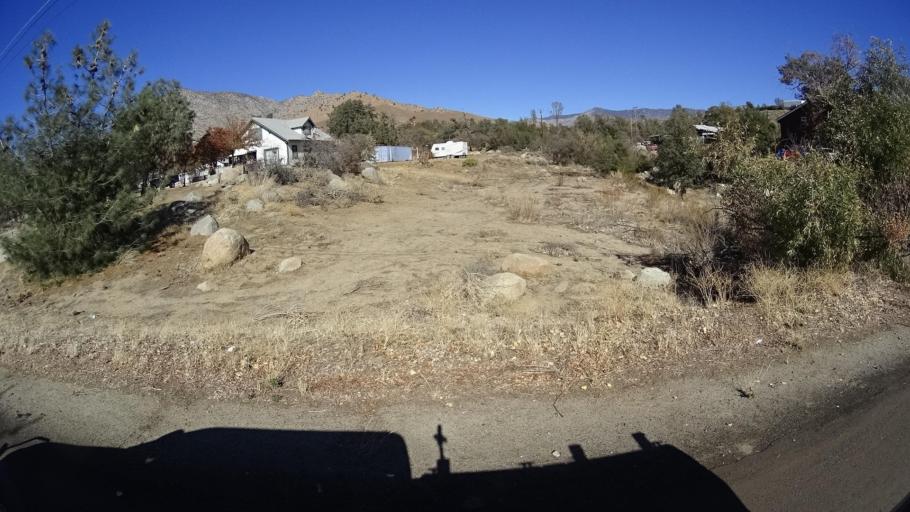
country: US
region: California
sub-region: Kern County
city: Wofford Heights
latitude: 35.7058
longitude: -118.4480
